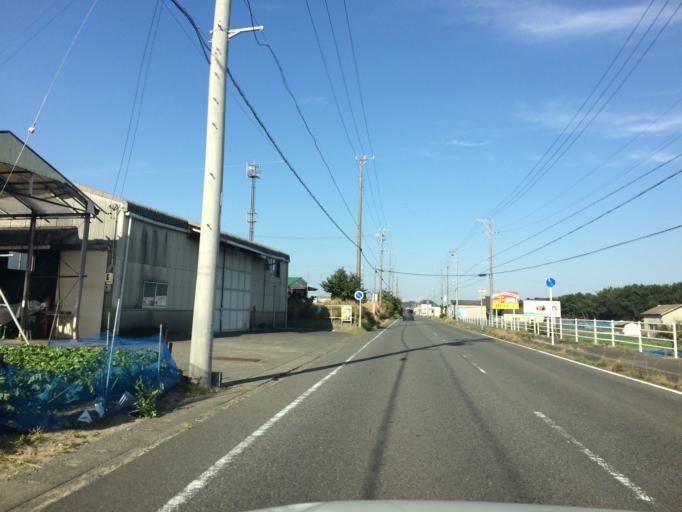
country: JP
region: Shizuoka
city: Sagara
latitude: 34.6686
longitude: 138.1951
